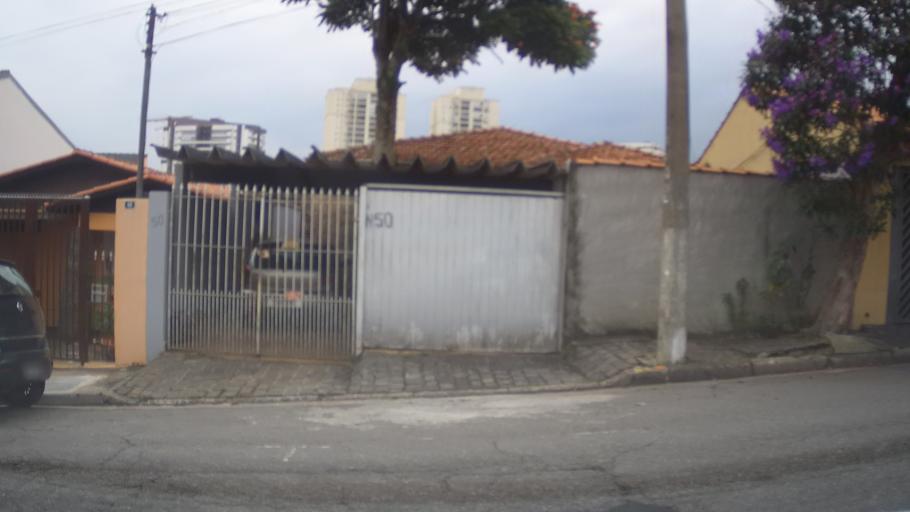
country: BR
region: Sao Paulo
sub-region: Guarulhos
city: Guarulhos
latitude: -23.4507
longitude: -46.5527
